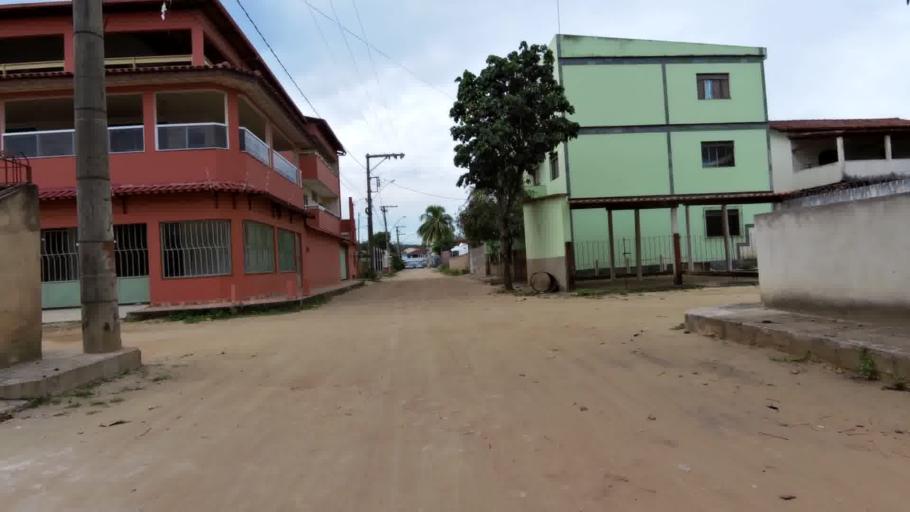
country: BR
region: Espirito Santo
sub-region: Piuma
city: Piuma
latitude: -20.8414
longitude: -40.7336
